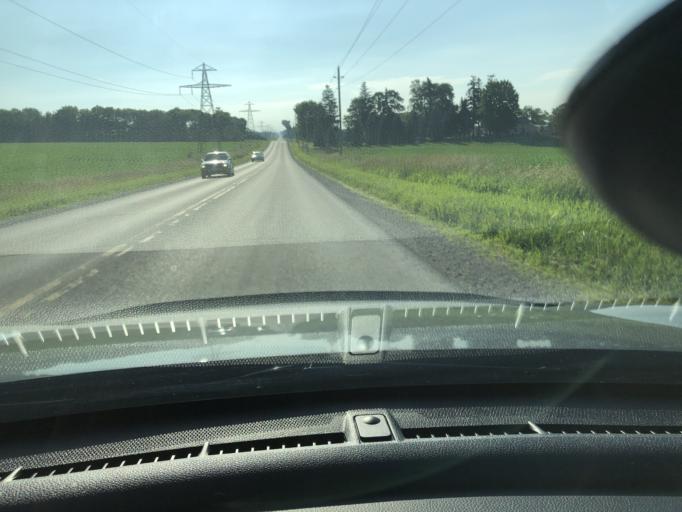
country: CA
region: Ontario
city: Stratford
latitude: 43.3885
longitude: -80.9124
